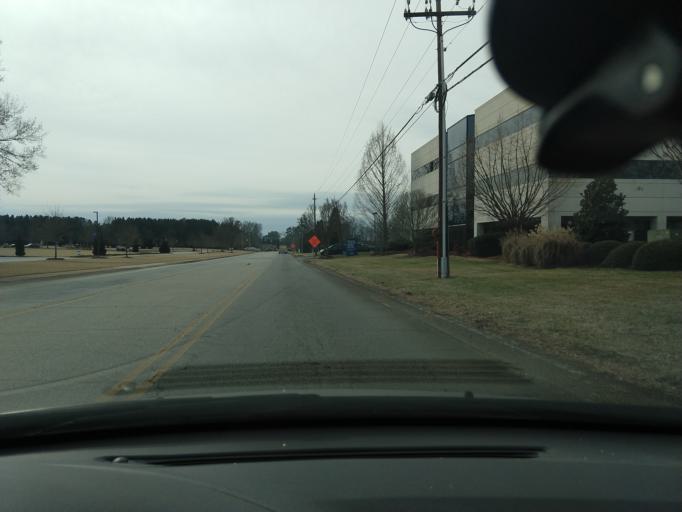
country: US
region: South Carolina
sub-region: Spartanburg County
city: Spartanburg
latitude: 34.9783
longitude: -81.8937
